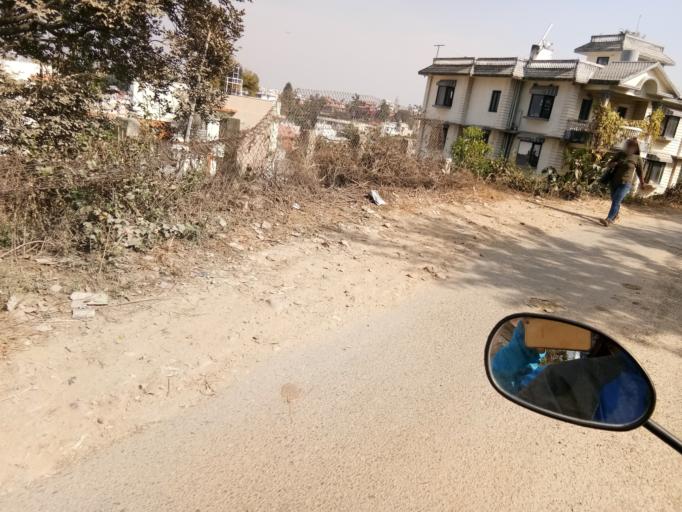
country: NP
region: Central Region
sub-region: Bagmati Zone
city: Patan
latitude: 27.6533
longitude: 85.2983
